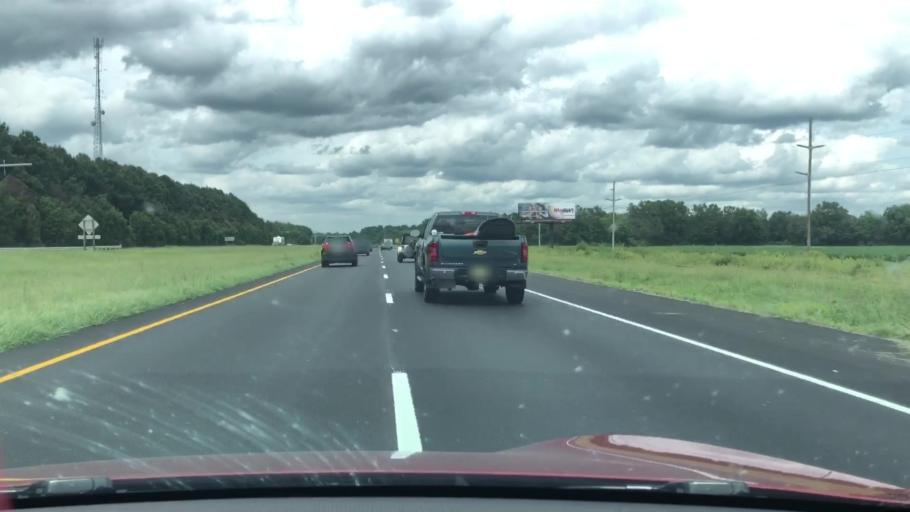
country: US
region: Maryland
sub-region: Somerset County
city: Princess Anne
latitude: 38.1564
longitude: -75.6913
